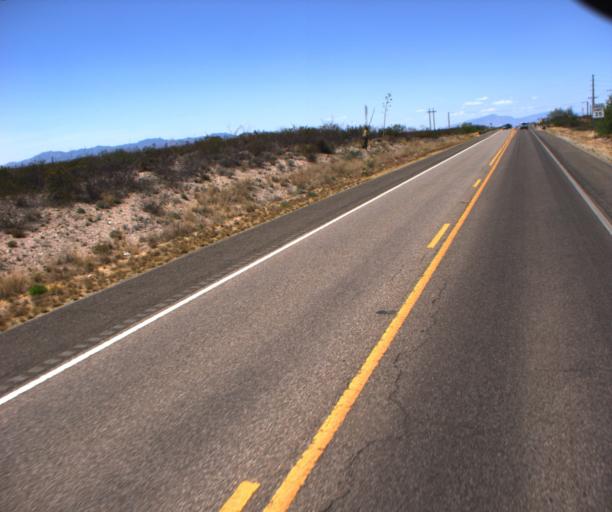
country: US
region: Arizona
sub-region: Cochise County
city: Tombstone
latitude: 31.7454
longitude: -110.0937
